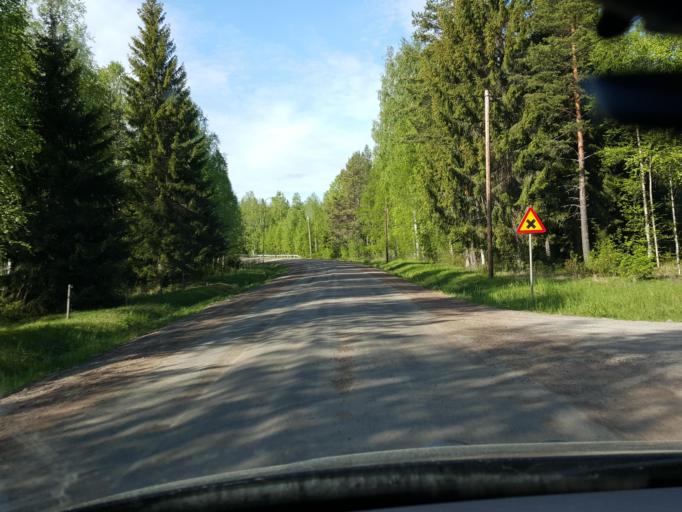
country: SE
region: Vaesternorrland
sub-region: Ange Kommun
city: Ange
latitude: 62.1819
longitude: 15.6343
